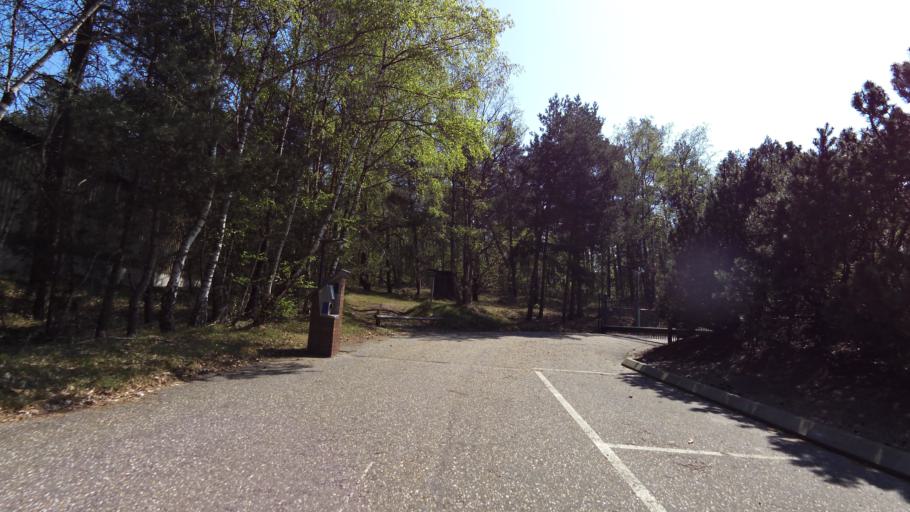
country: NL
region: Gelderland
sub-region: Gemeente Renkum
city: Wolfheze
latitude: 52.0214
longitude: 5.8102
